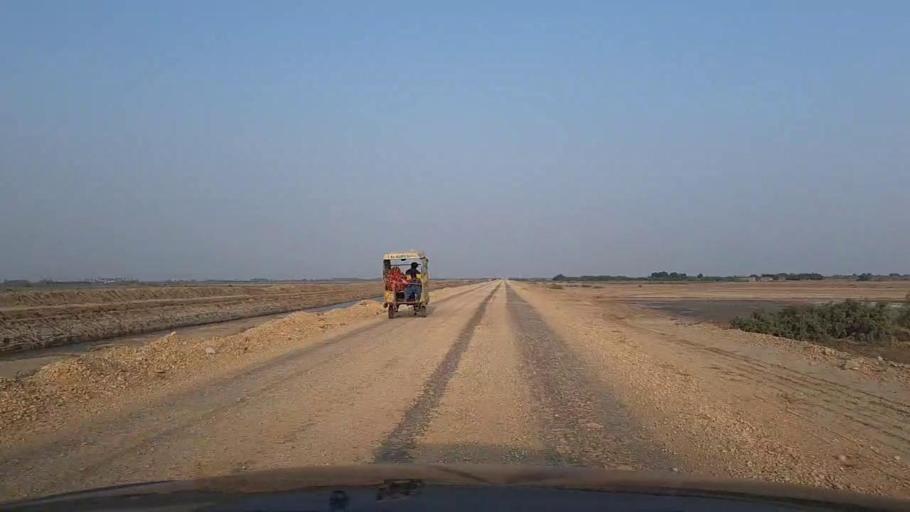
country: PK
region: Sindh
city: Mirpur Sakro
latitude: 24.4365
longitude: 67.7694
